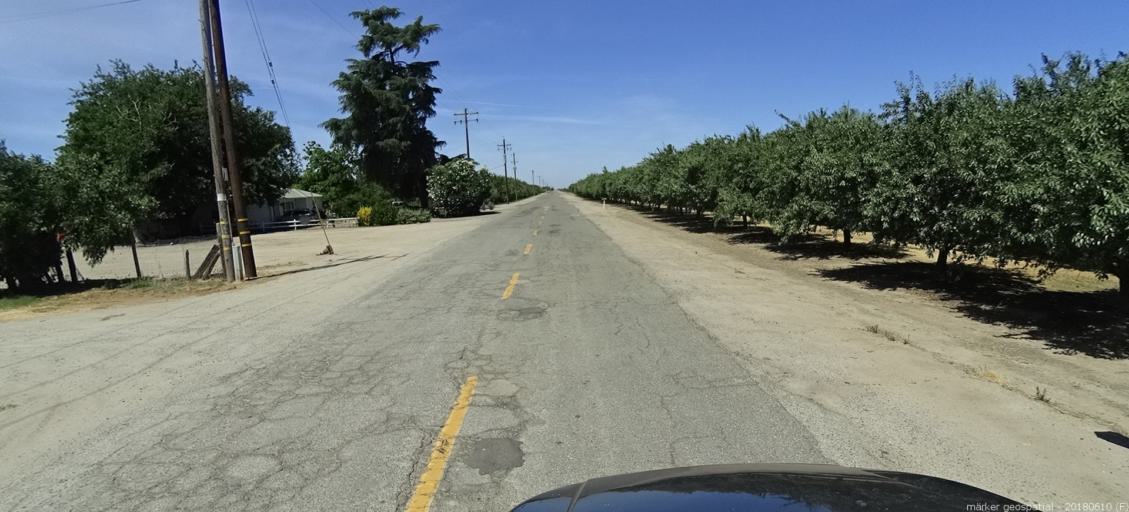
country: US
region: California
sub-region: Madera County
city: Chowchilla
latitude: 37.0545
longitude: -120.4031
